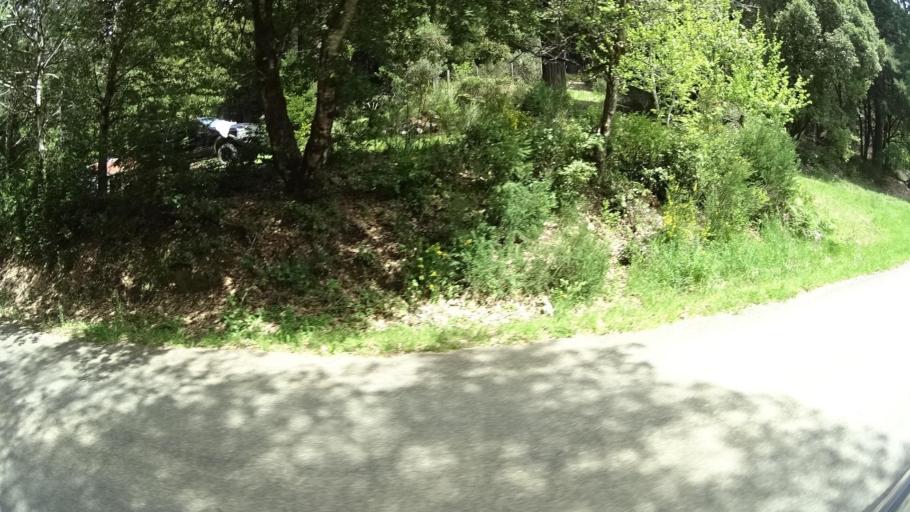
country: US
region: California
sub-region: Humboldt County
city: Redway
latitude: 40.0229
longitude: -123.9414
